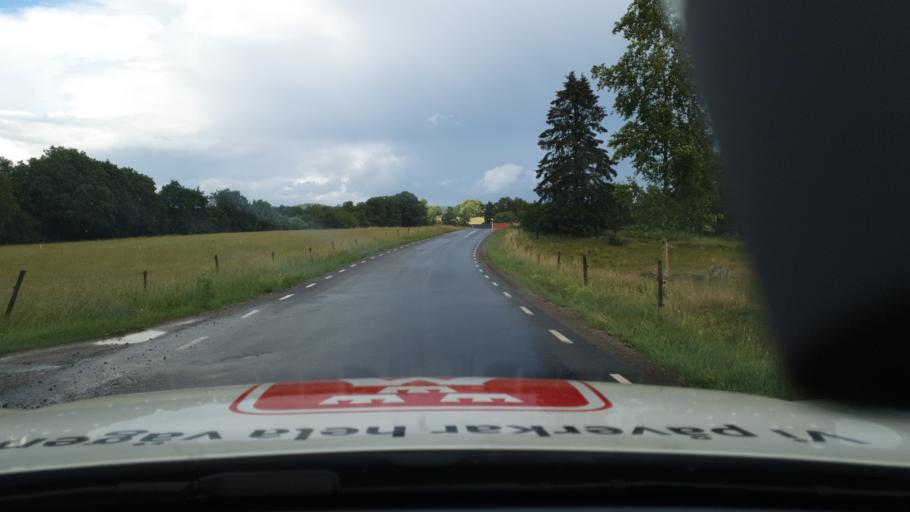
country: SE
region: Vaestra Goetaland
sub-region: Falkopings Kommun
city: Falkoeping
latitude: 58.0633
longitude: 13.6250
